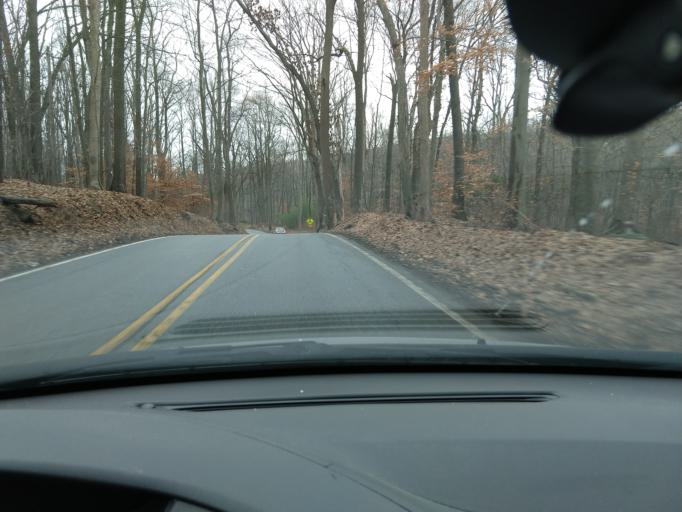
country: US
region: Pennsylvania
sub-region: Montgomery County
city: Stowe
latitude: 40.1964
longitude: -75.6945
